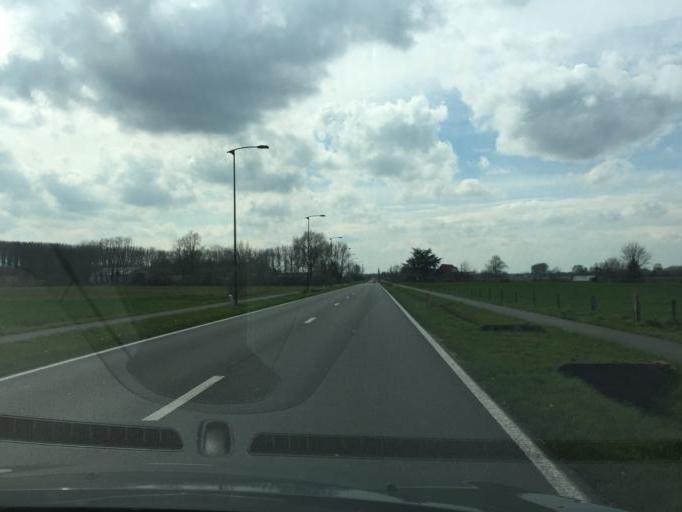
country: BE
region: Flanders
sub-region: Provincie Oost-Vlaanderen
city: Aalter
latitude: 51.0628
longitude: 3.4284
